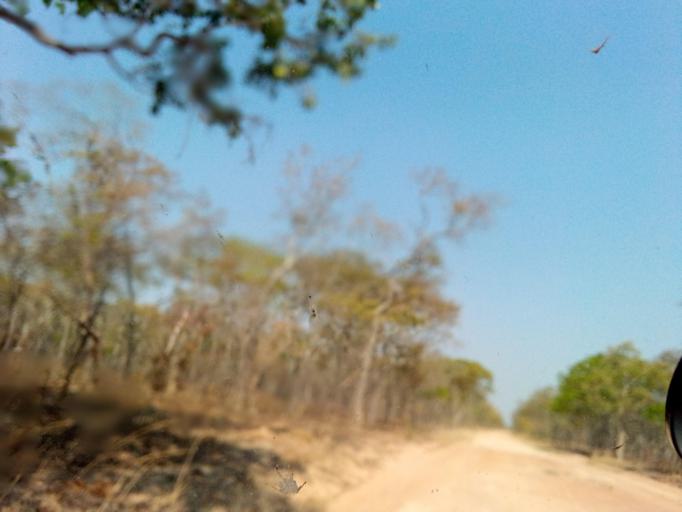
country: ZM
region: Northern
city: Mpika
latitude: -12.2422
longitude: 30.8370
